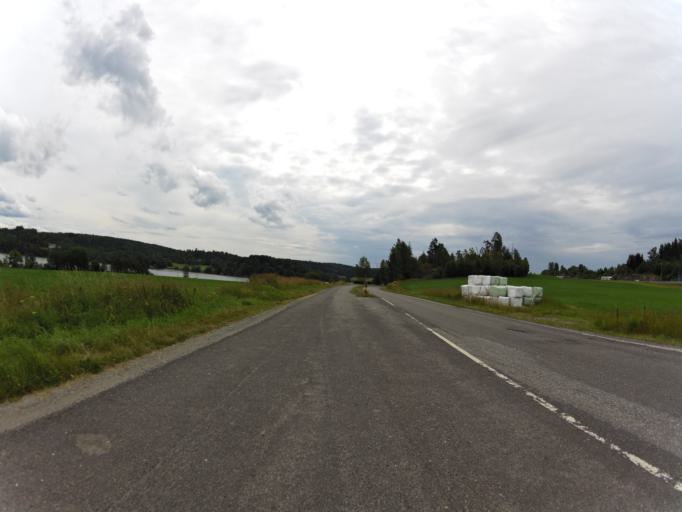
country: NO
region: Akershus
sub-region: As
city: As
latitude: 59.6858
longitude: 10.7394
